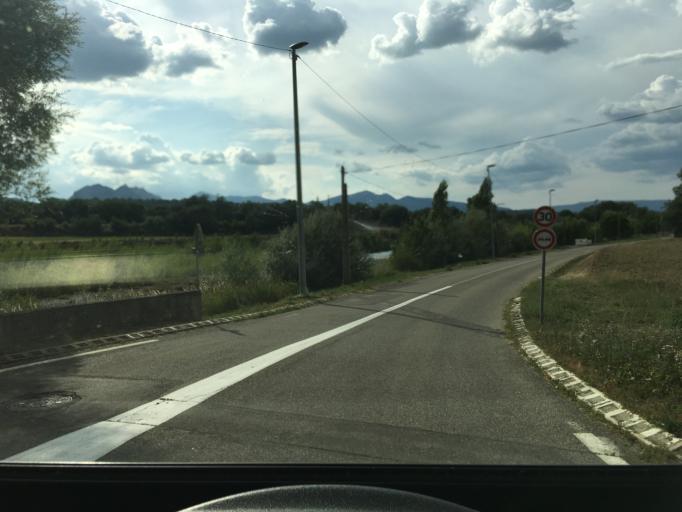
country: FR
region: Provence-Alpes-Cote d'Azur
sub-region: Departement des Alpes-de-Haute-Provence
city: Sisteron
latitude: 44.2116
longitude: 5.9405
